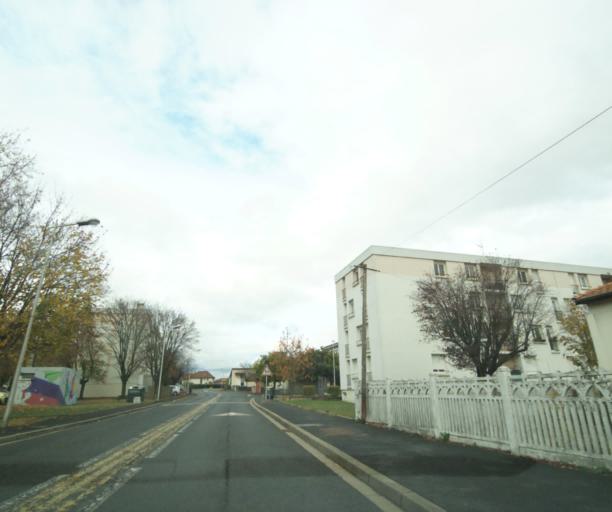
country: FR
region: Auvergne
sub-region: Departement du Puy-de-Dome
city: Pont-du-Chateau
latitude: 45.8026
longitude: 3.2440
